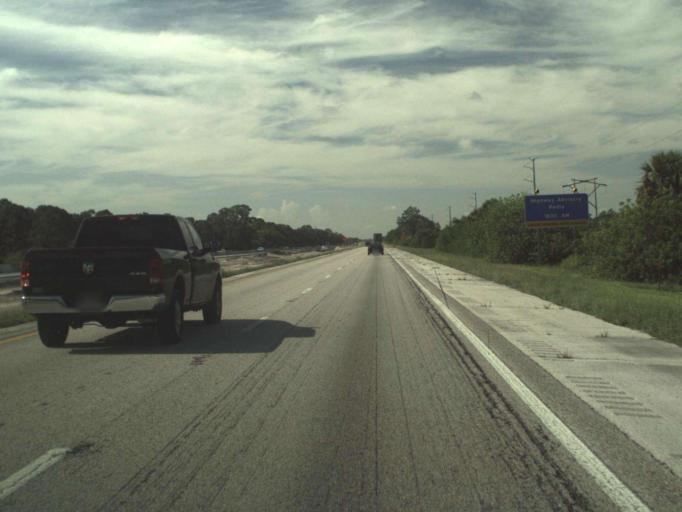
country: US
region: Florida
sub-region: Indian River County
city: West Vero Corridor
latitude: 27.6992
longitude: -80.5397
